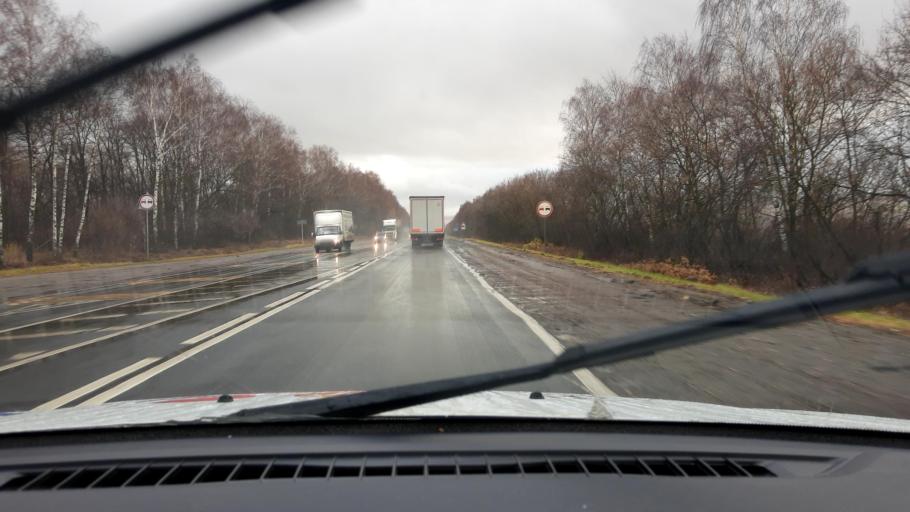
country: RU
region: Nizjnij Novgorod
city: Pamyat' Parizhskoy Kommuny
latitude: 56.0558
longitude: 44.3998
